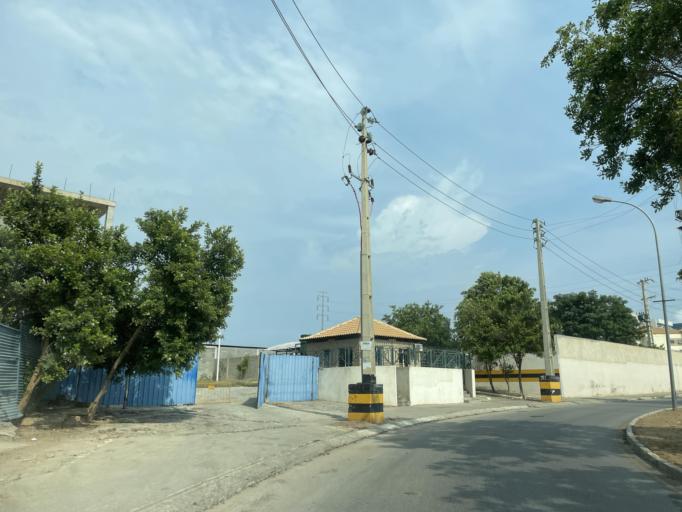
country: AO
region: Luanda
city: Luanda
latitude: -8.9199
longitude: 13.1868
